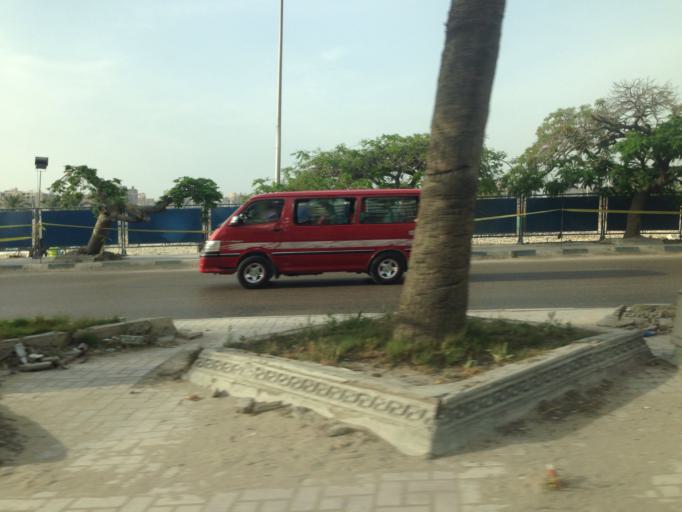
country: EG
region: Alexandria
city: Alexandria
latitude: 31.2126
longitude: 29.9522
